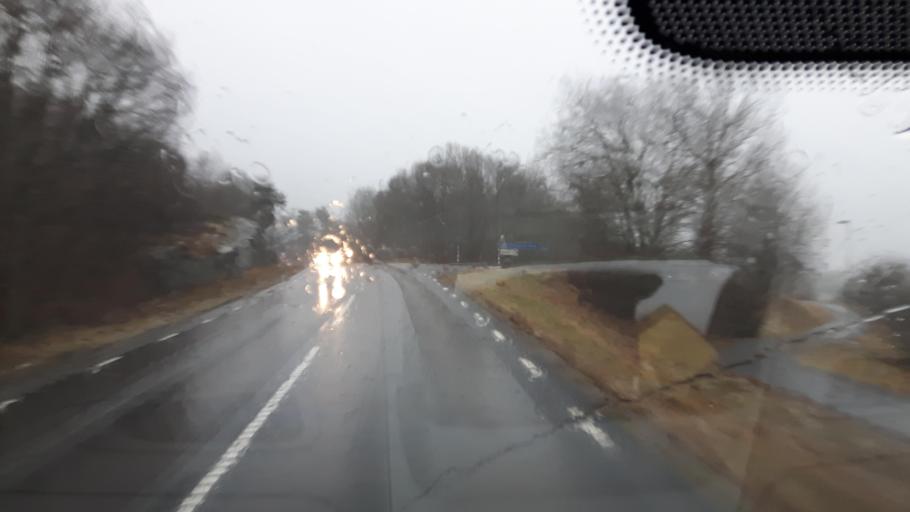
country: SE
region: Halland
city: Saro
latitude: 57.4379
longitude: 11.9358
